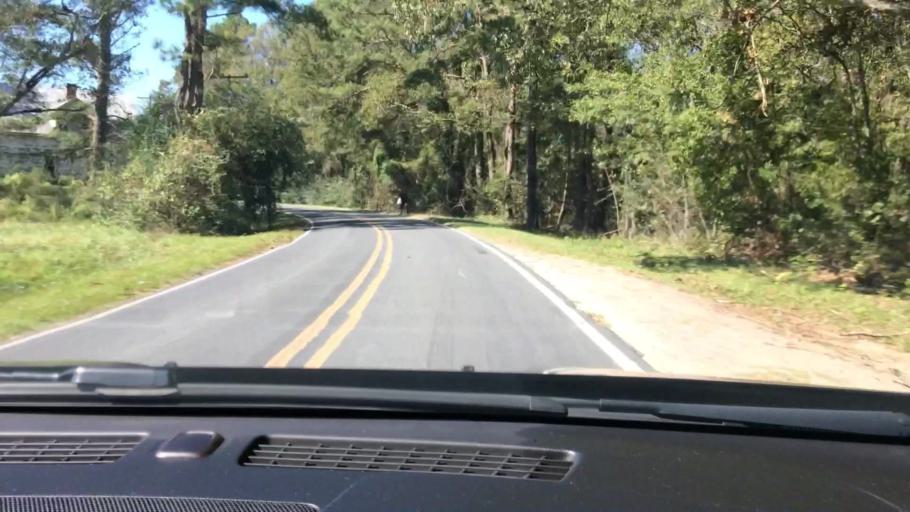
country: US
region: North Carolina
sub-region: Pitt County
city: Grifton
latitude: 35.2927
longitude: -77.3337
